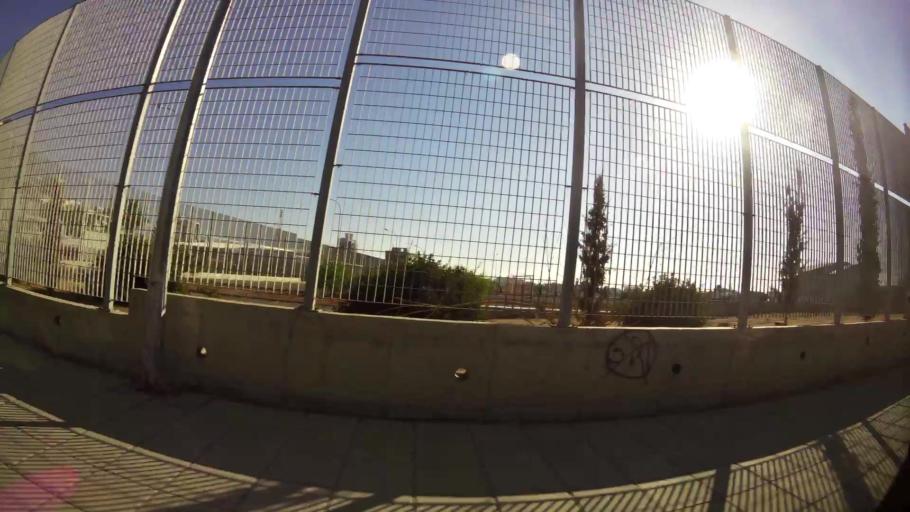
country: CY
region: Larnaka
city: Larnaca
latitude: 34.9288
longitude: 33.6211
